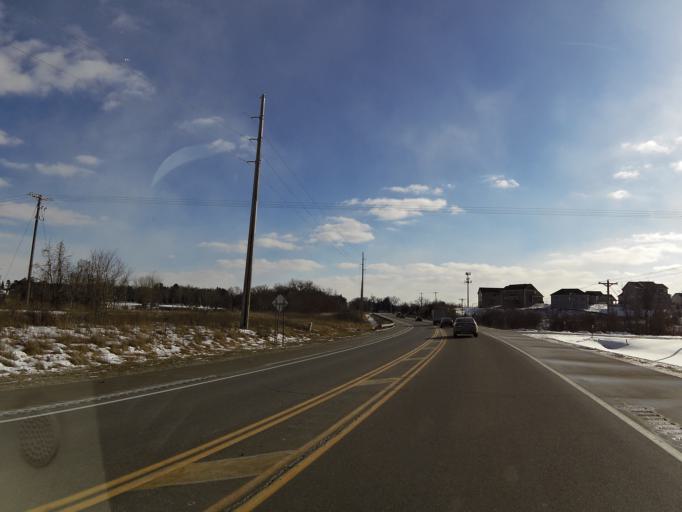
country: US
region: Minnesota
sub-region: Dakota County
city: Rosemount
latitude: 44.7800
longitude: -93.1165
